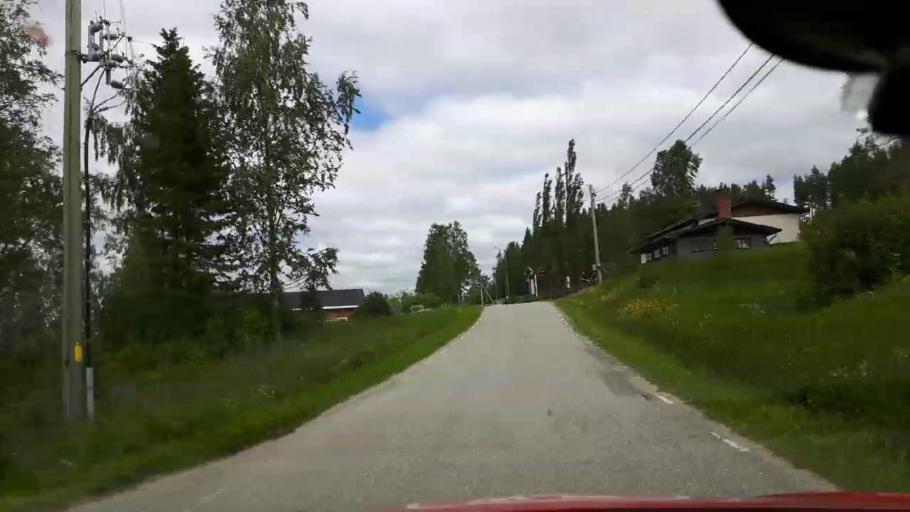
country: SE
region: Jaemtland
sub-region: Braecke Kommun
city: Braecke
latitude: 62.8684
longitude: 15.2719
